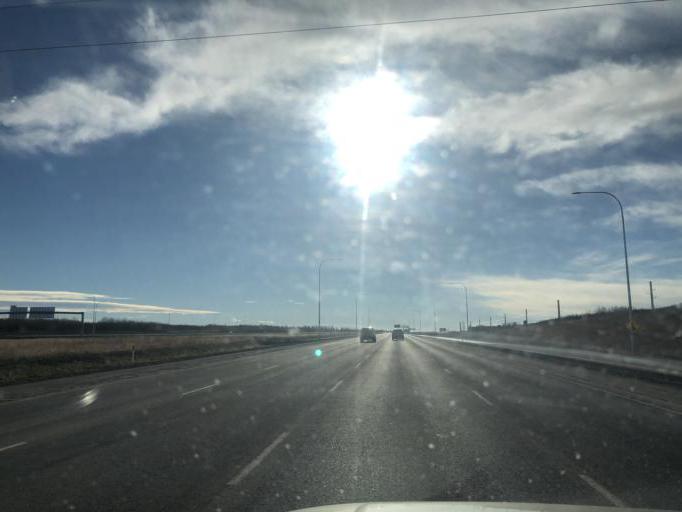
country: CA
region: Alberta
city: Calgary
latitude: 50.9712
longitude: -114.1536
